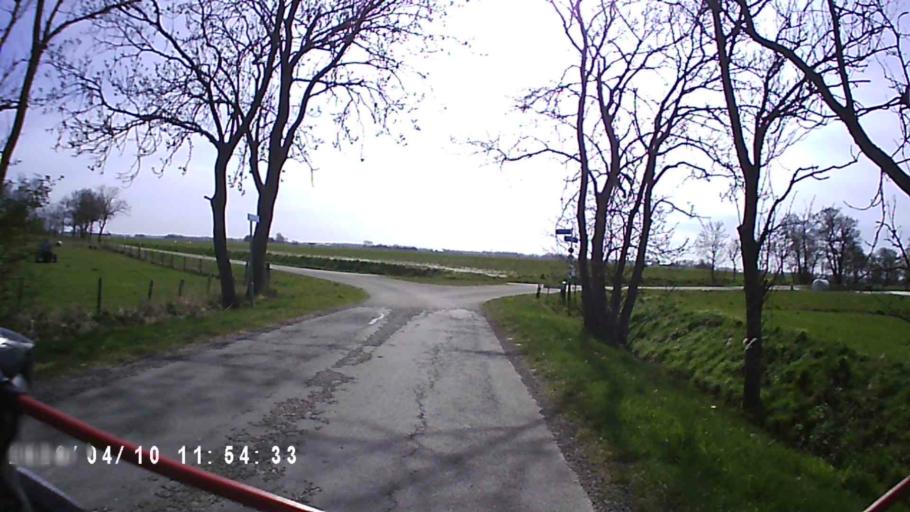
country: NL
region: Groningen
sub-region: Gemeente De Marne
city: Ulrum
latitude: 53.3860
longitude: 6.3370
